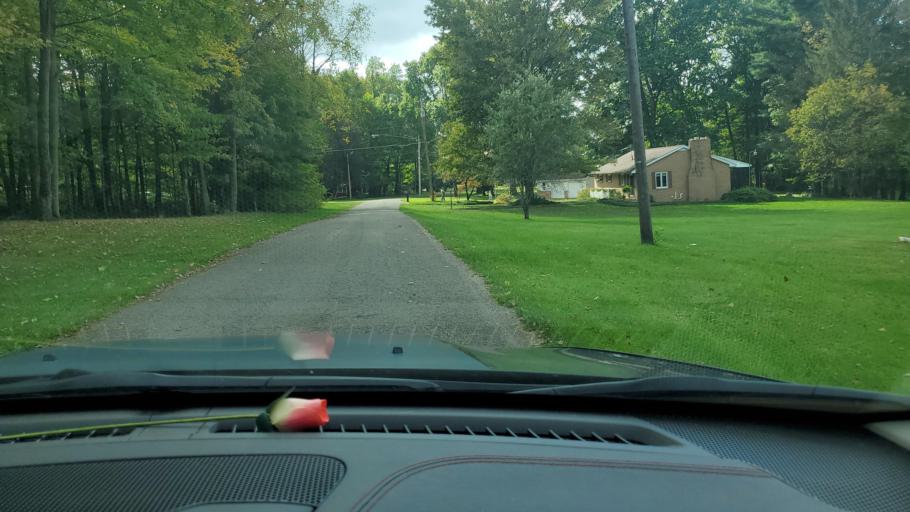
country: US
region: Ohio
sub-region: Ashtabula County
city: Andover
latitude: 41.4526
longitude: -80.5764
